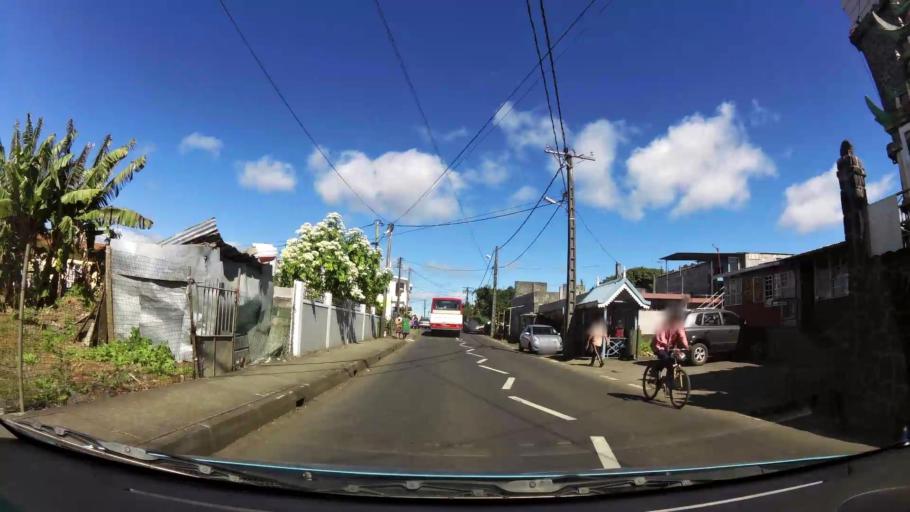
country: MU
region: Plaines Wilhems
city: Vacoas
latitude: -20.3310
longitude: 57.4755
